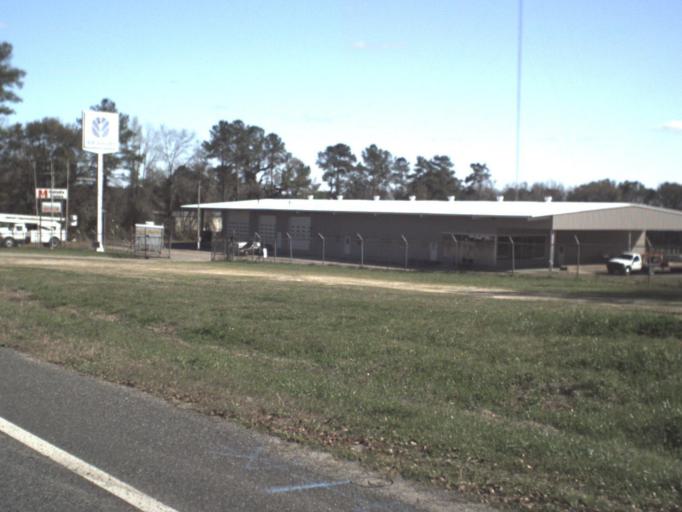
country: US
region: Florida
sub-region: Gadsden County
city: Midway
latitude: 30.4955
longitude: -84.4335
